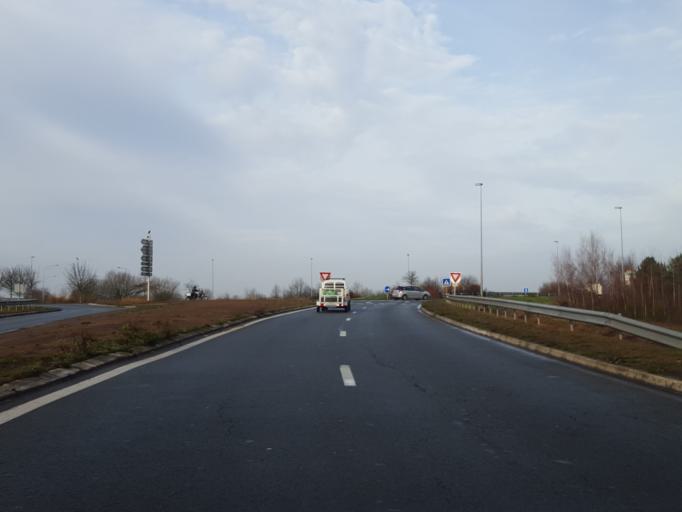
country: FR
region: Pays de la Loire
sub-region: Departement de la Vendee
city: La Roche-sur-Yon
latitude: 46.6776
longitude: -1.3976
